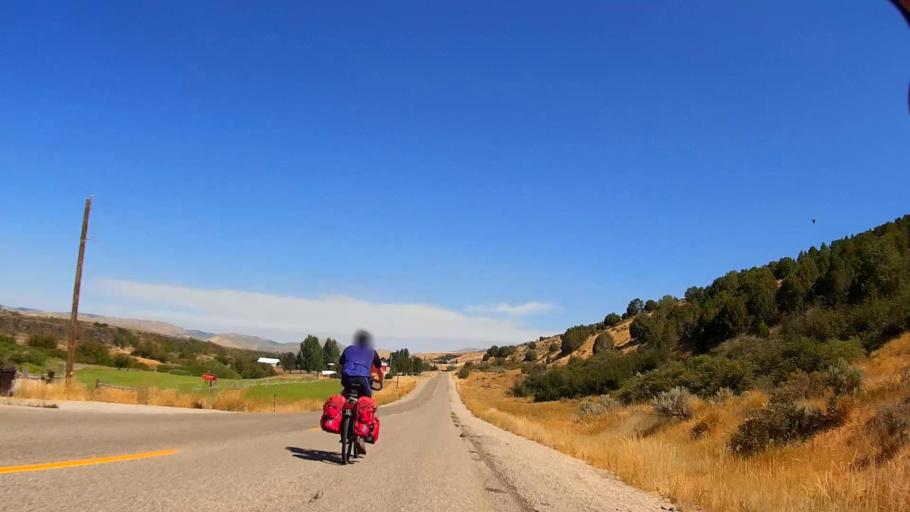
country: US
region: Idaho
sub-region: Bannock County
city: Pocatello
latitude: 42.7136
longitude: -112.2078
